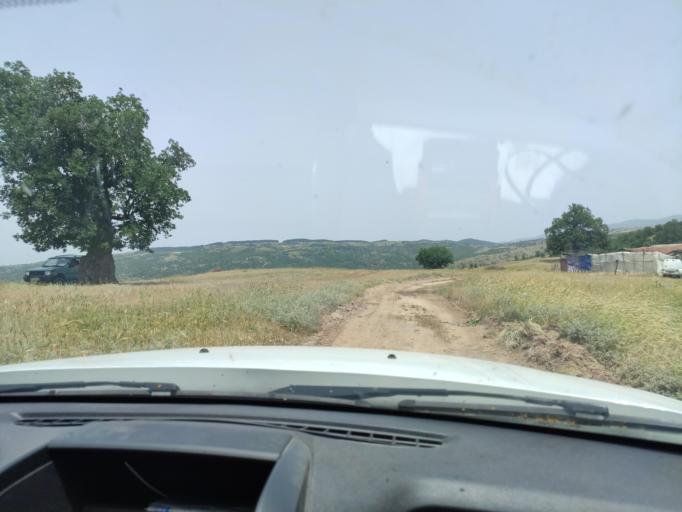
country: MK
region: Radovis
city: Radovish
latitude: 41.6777
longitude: 22.3985
